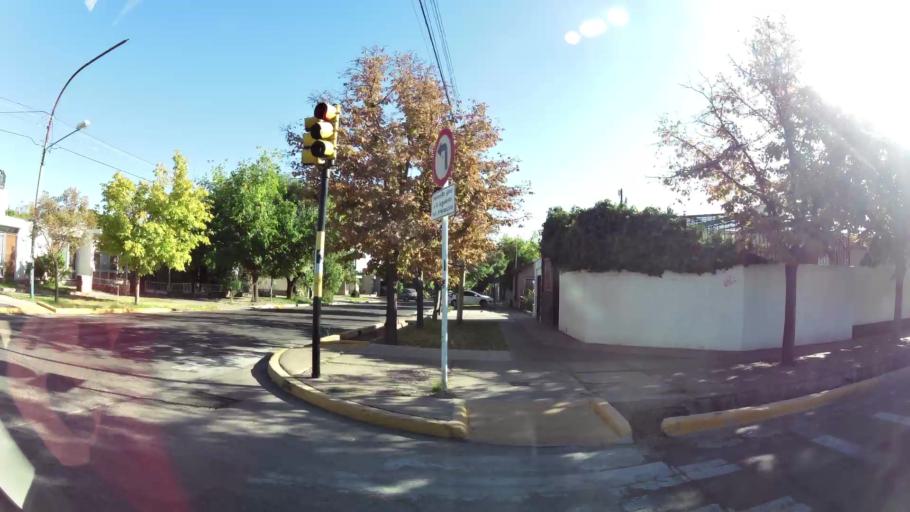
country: AR
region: Mendoza
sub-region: Departamento de Godoy Cruz
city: Godoy Cruz
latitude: -32.9308
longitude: -68.8354
